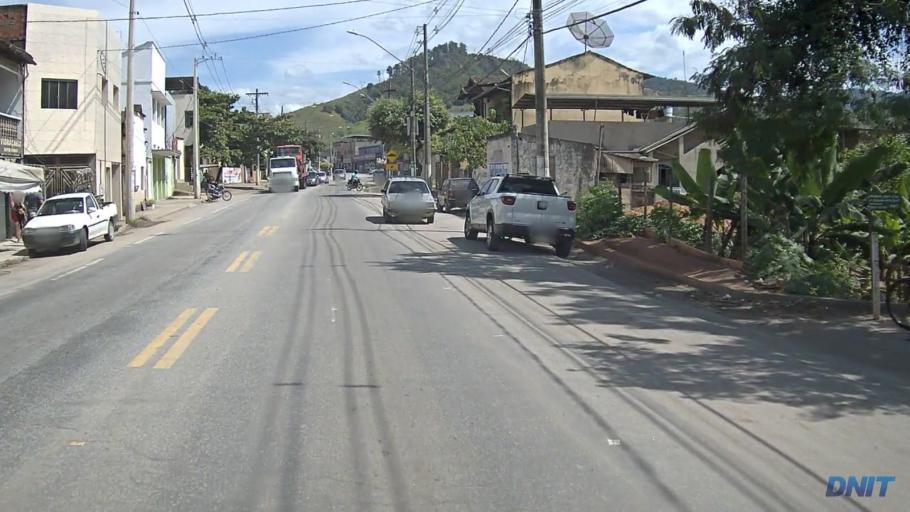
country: BR
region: Minas Gerais
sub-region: Coronel Fabriciano
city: Coronel Fabriciano
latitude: -19.5304
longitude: -42.6644
